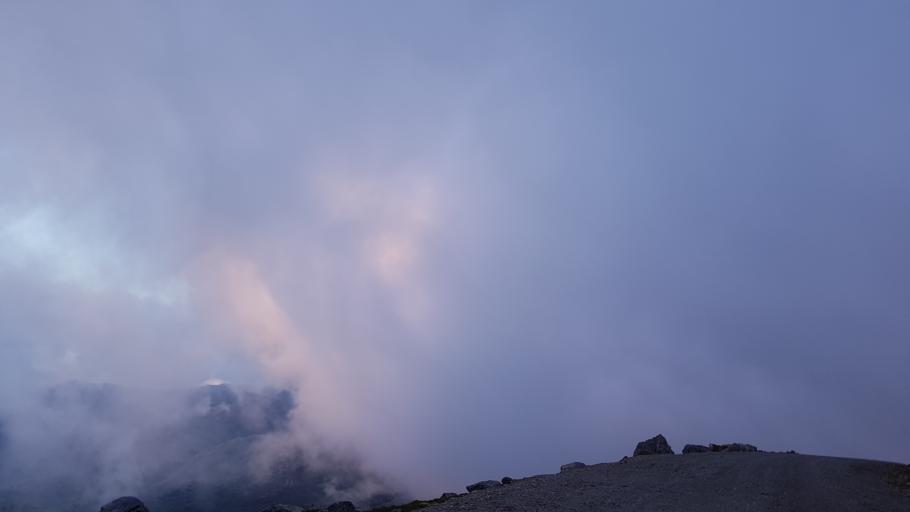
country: GR
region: Crete
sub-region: Nomos Chanias
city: Vryses
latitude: 35.4275
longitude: 23.6075
